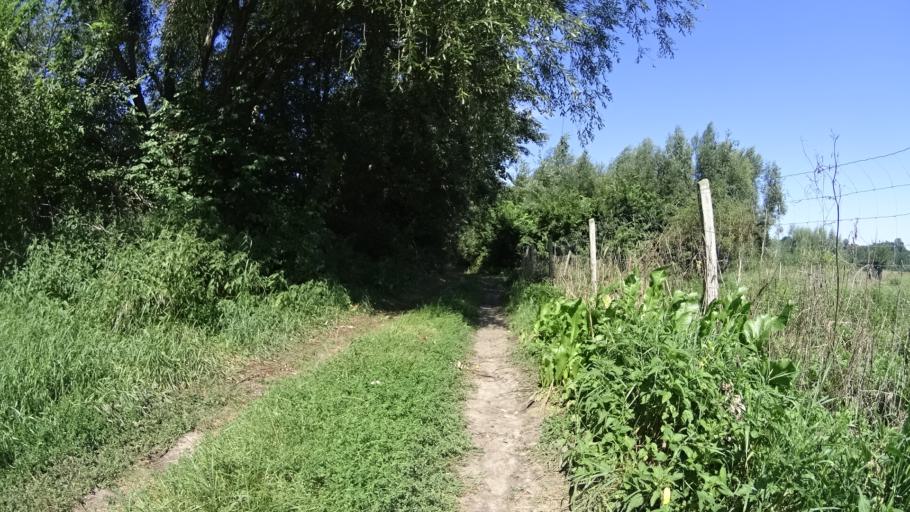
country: PL
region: Masovian Voivodeship
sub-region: Powiat bialobrzeski
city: Wysmierzyce
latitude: 51.6629
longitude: 20.8756
